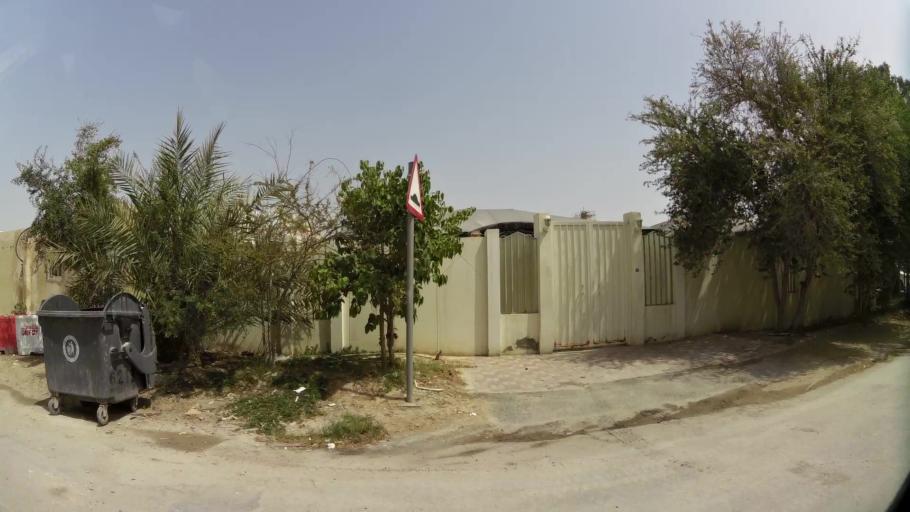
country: QA
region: Baladiyat ar Rayyan
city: Ar Rayyan
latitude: 25.2356
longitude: 51.4163
